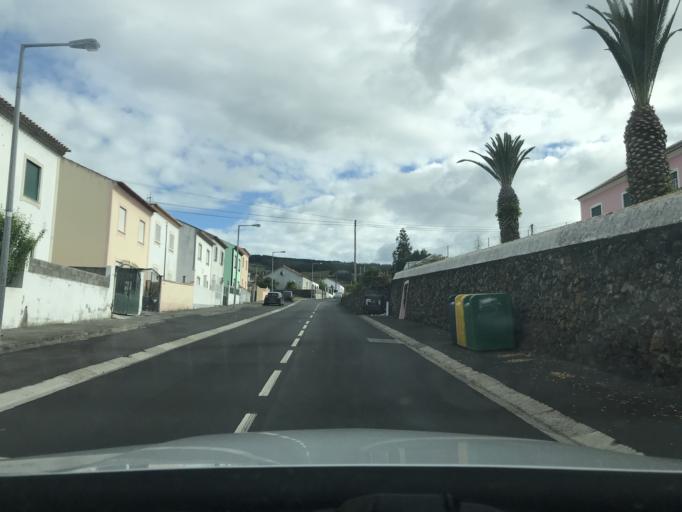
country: PT
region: Azores
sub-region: Angra do Heroismo
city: Angra do Heroismo
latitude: 38.6694
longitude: -27.2515
